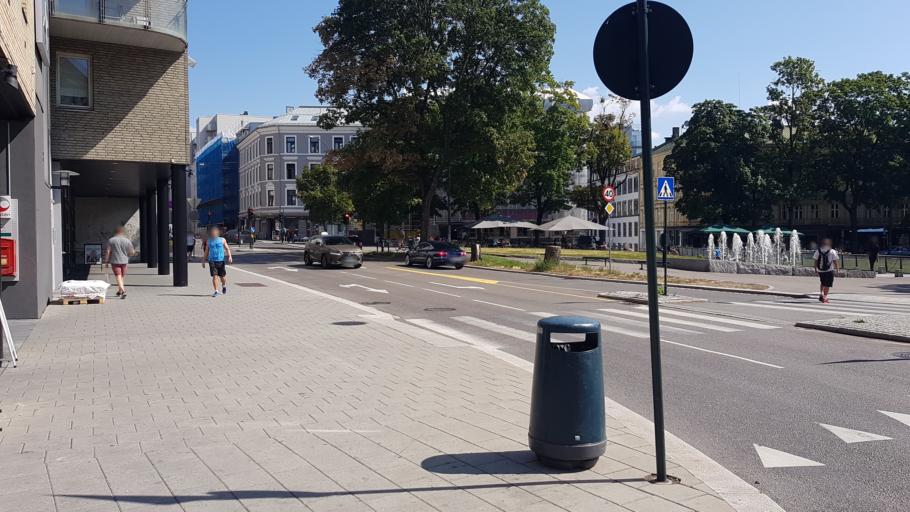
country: NO
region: Oslo
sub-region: Oslo
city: Oslo
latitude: 59.9282
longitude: 10.7500
